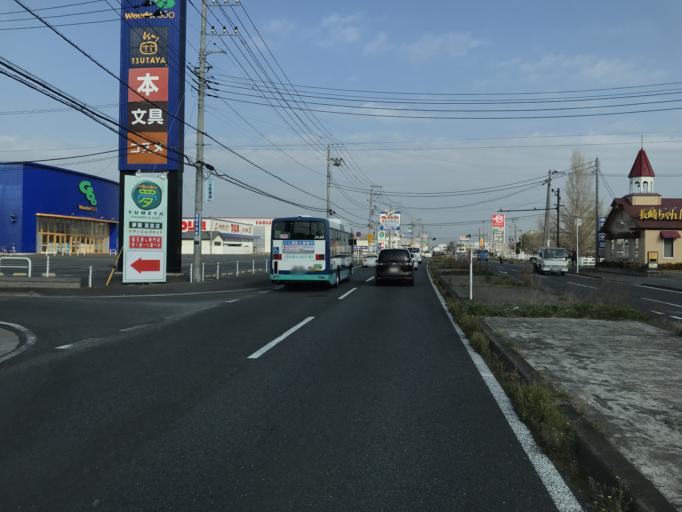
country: JP
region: Chiba
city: Narita
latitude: 35.7482
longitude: 140.3106
